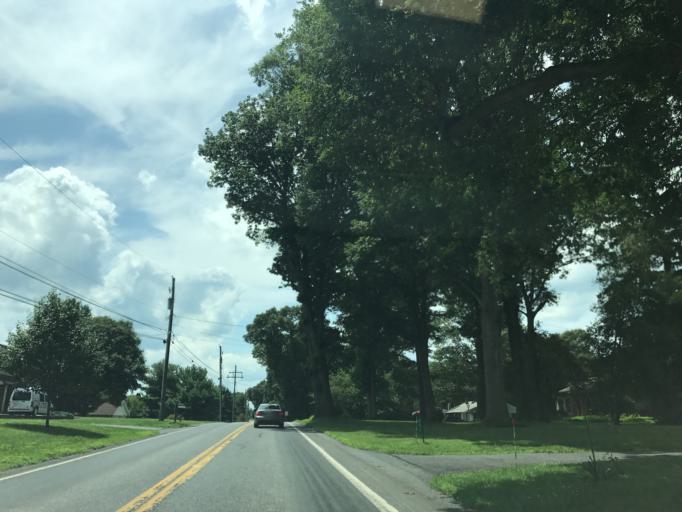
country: US
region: Pennsylvania
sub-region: Lancaster County
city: Penryn
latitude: 40.2082
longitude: -76.3368
